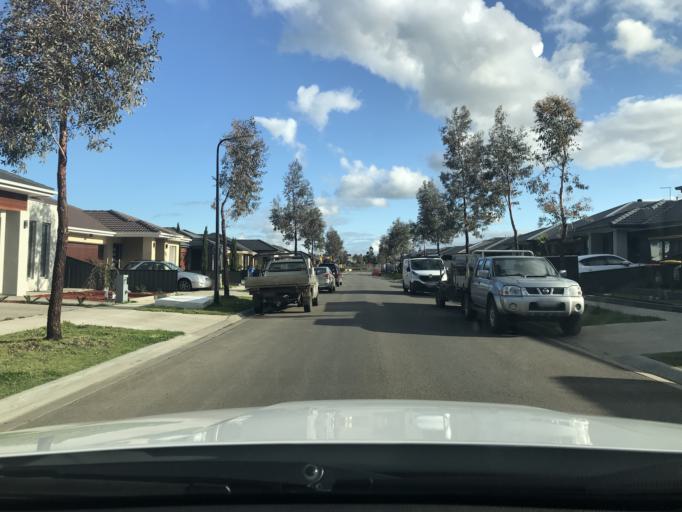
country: AU
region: Victoria
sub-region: Hume
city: Roxburgh Park
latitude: -37.5898
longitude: 144.8960
